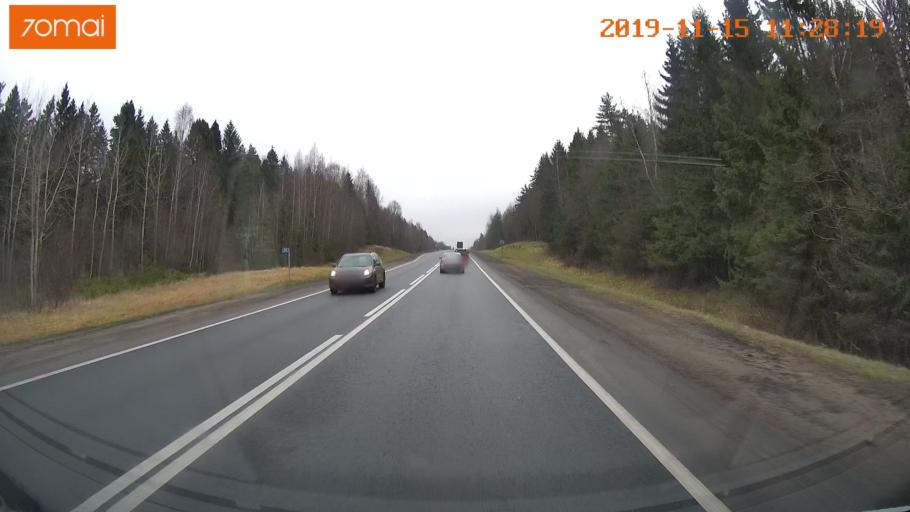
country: RU
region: Vologda
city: Molochnoye
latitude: 59.1721
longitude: 39.4853
